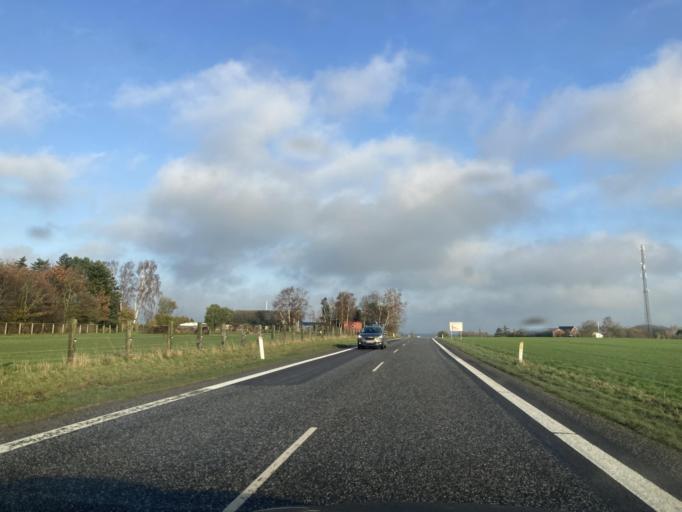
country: DK
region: Zealand
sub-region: Lolland Kommune
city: Rodby
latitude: 54.6906
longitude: 11.3702
